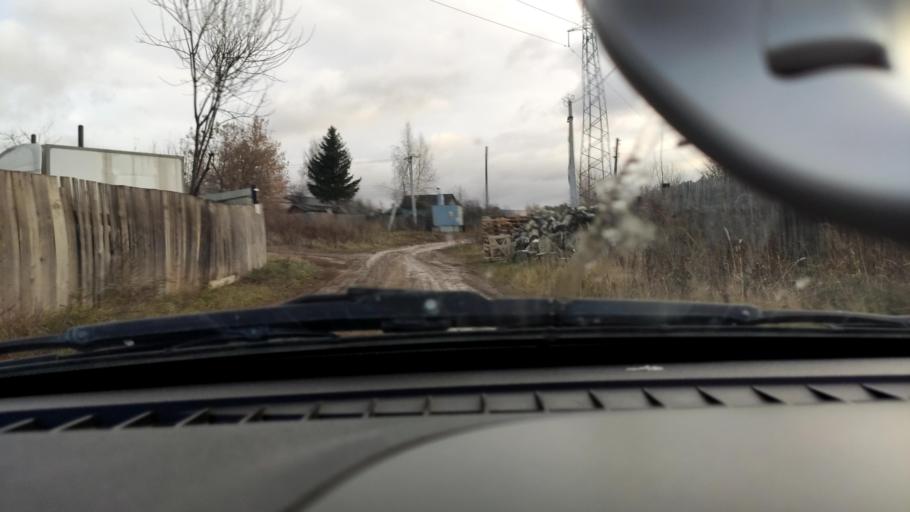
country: RU
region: Perm
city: Kondratovo
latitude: 57.9558
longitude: 56.1466
